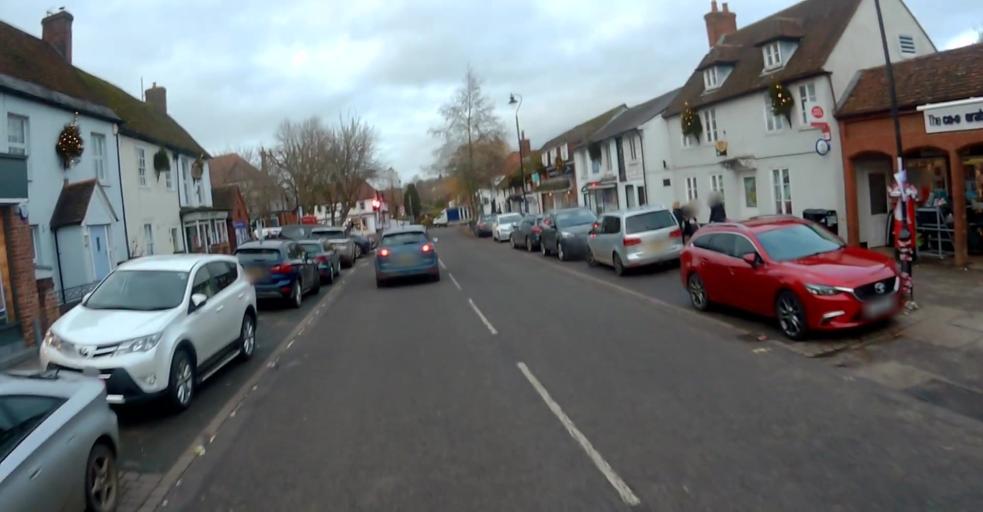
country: GB
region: England
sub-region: Hampshire
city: Overton
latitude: 51.2433
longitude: -1.2630
